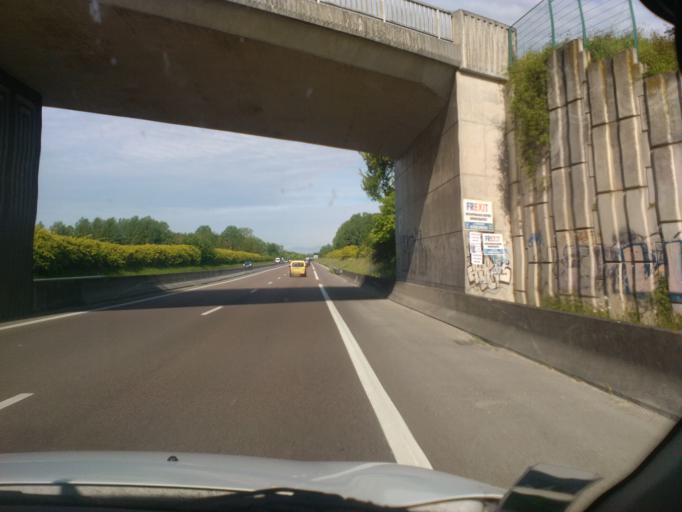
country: FR
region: Champagne-Ardenne
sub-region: Departement de l'Aube
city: Sainte-Maure
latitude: 48.3278
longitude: 4.0672
